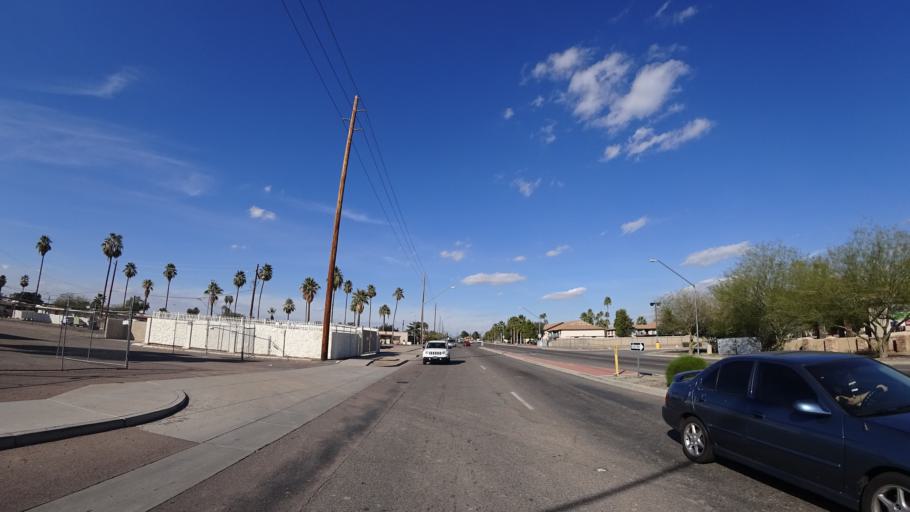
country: US
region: Arizona
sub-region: Maricopa County
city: Glendale
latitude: 33.5390
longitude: -112.2206
